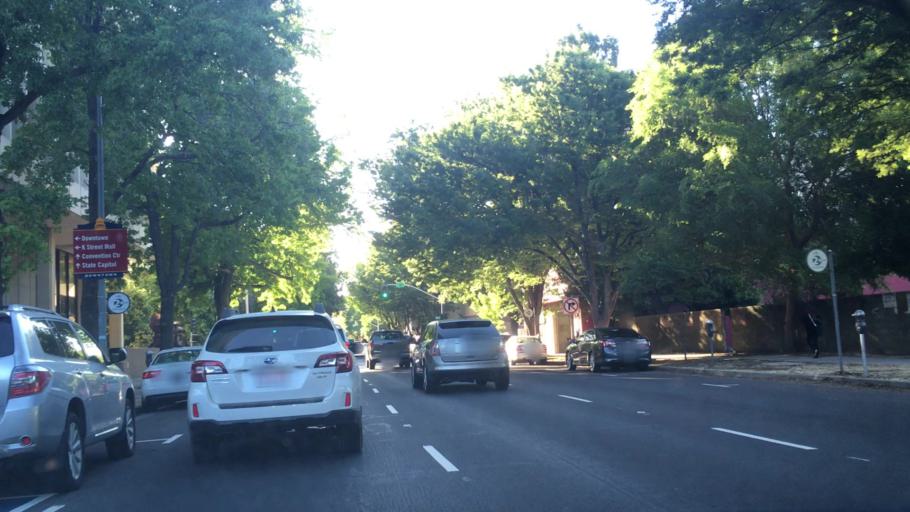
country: US
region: California
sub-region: Sacramento County
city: Sacramento
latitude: 38.5736
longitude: -121.5004
